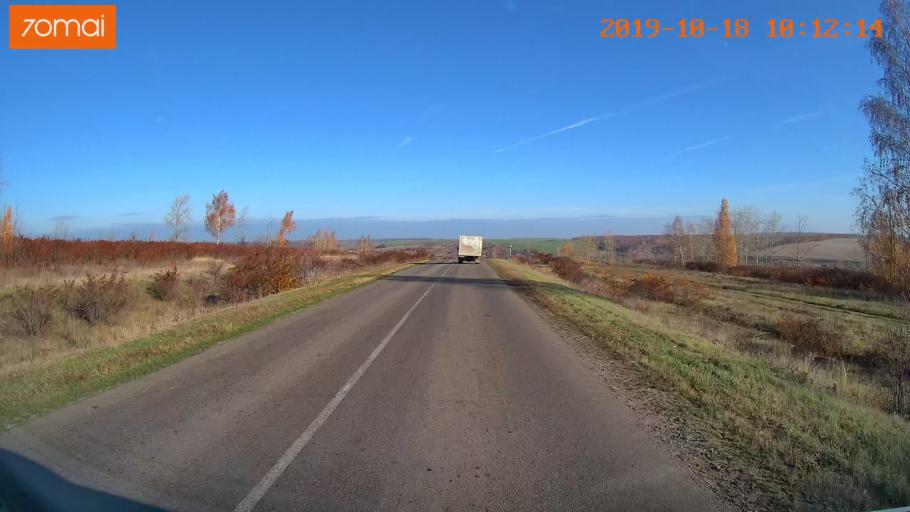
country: RU
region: Tula
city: Kurkino
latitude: 53.3917
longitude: 38.5061
